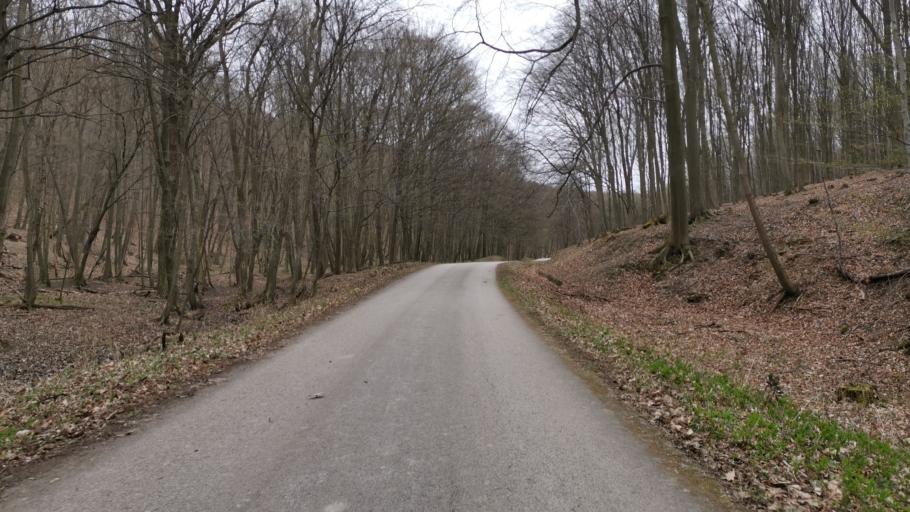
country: CZ
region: South Moravian
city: Petrov
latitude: 48.8146
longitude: 17.3163
